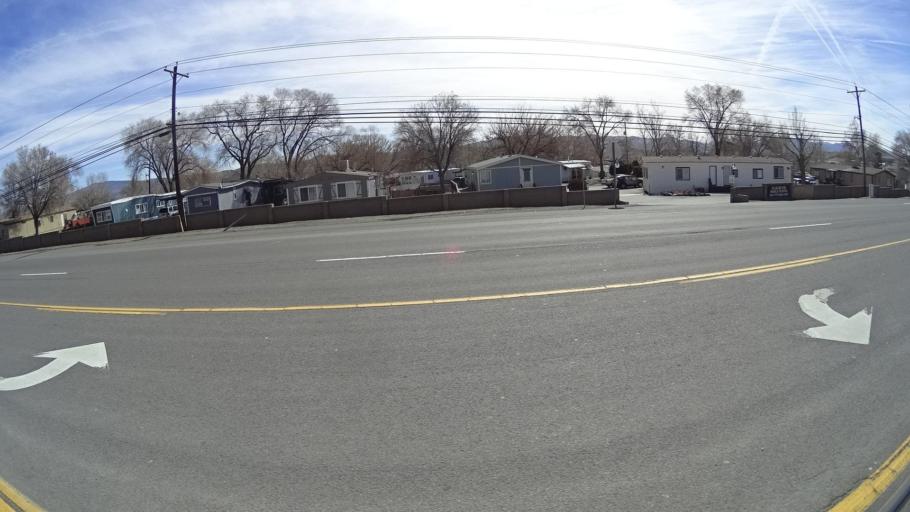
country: US
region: Nevada
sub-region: Washoe County
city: Sun Valley
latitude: 39.5867
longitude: -119.7418
